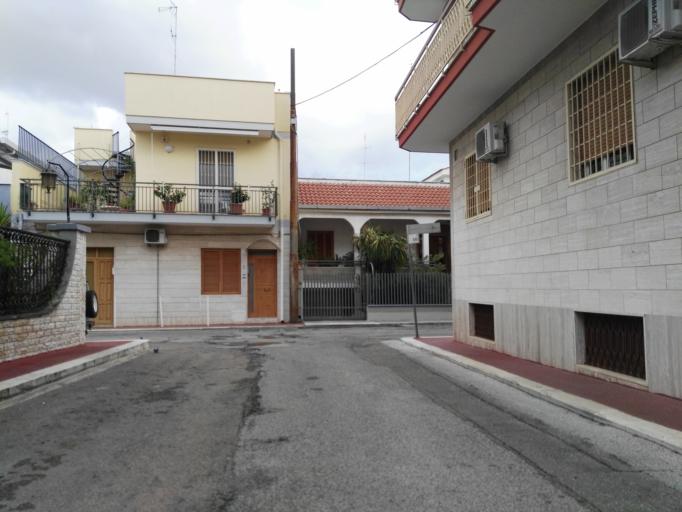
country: IT
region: Apulia
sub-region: Provincia di Bari
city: Triggiano
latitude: 41.0611
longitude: 16.9173
